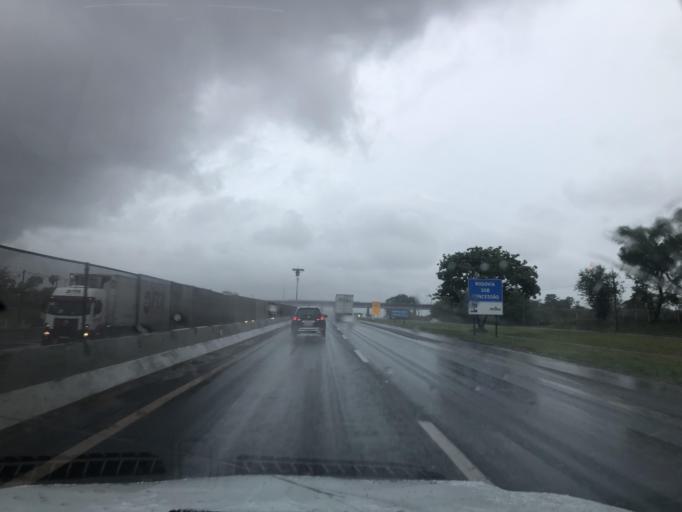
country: BR
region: Sao Paulo
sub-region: Ribeirao Preto
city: Ribeirao Preto
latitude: -21.1617
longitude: -47.7563
